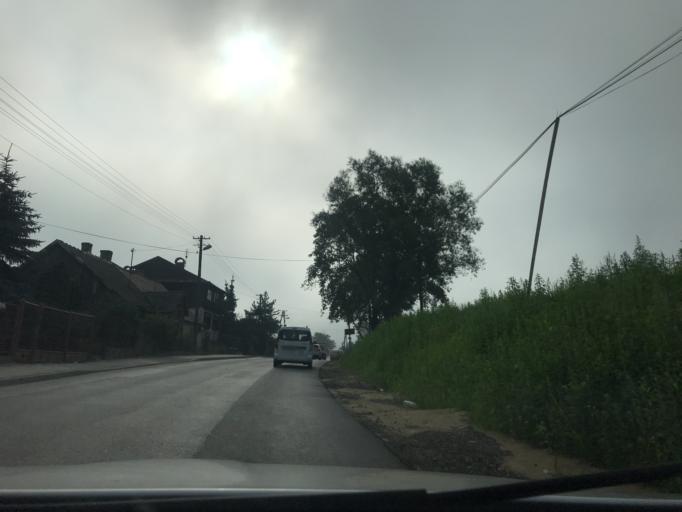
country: PL
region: Lesser Poland Voivodeship
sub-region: Powiat krakowski
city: Ochojno
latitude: 50.0040
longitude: 19.9921
